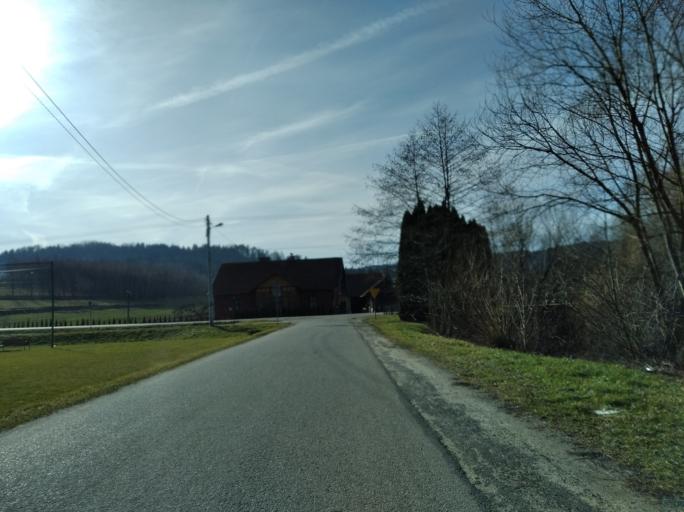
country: PL
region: Subcarpathian Voivodeship
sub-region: Powiat strzyzowski
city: Jawornik
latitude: 49.8159
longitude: 21.8416
